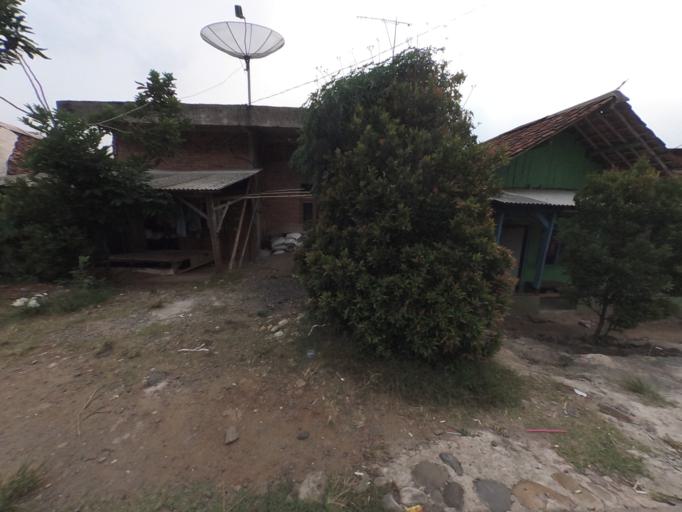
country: ID
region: West Java
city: Sidoger Lebak
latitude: -6.5628
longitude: 106.5829
